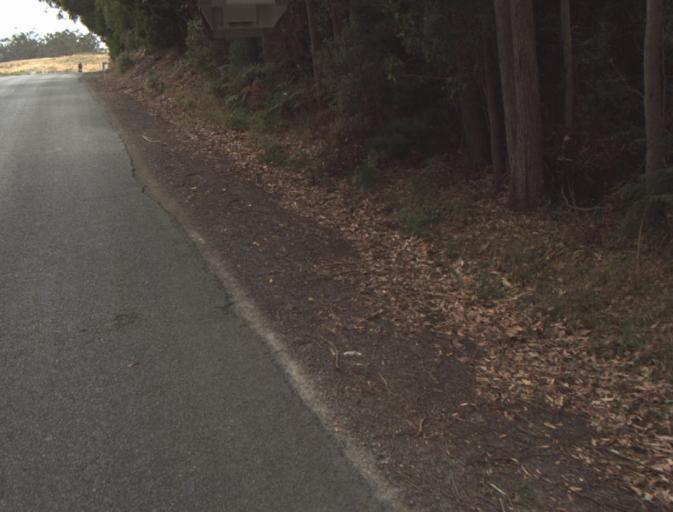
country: AU
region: Tasmania
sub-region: Launceston
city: Mayfield
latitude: -41.2111
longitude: 147.2130
